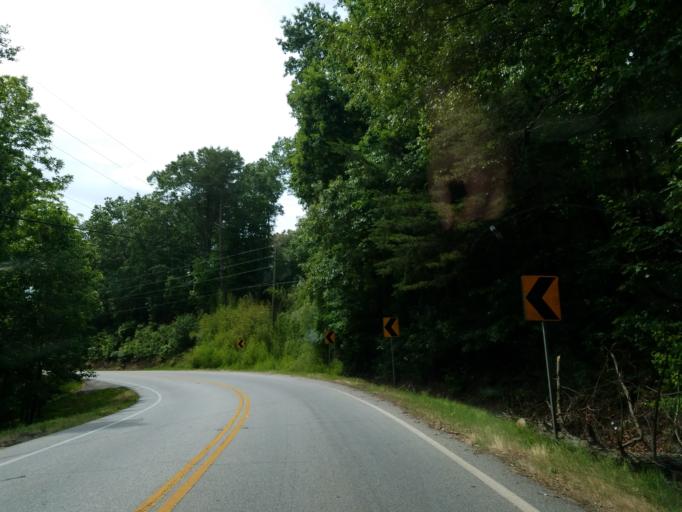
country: US
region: Georgia
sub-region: Lumpkin County
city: Dahlonega
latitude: 34.5264
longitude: -83.9214
